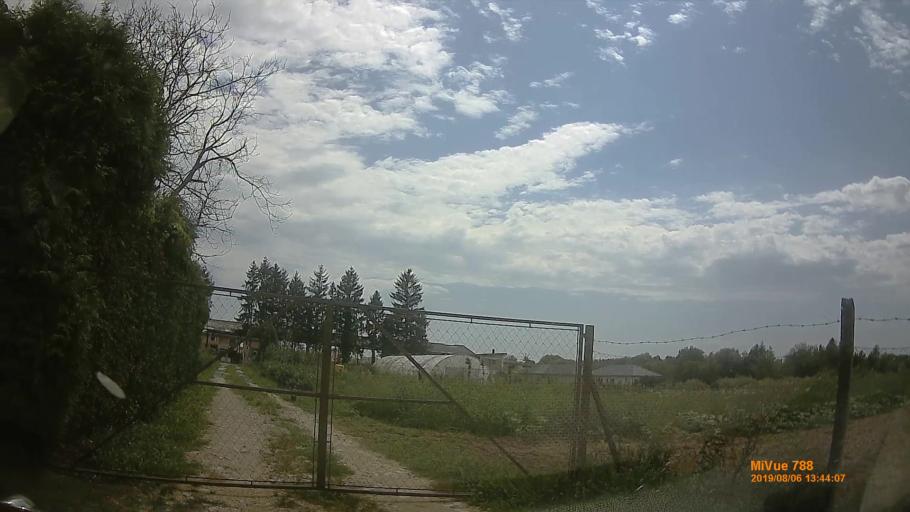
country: HU
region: Vas
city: Gencsapati
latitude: 47.2554
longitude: 16.5983
